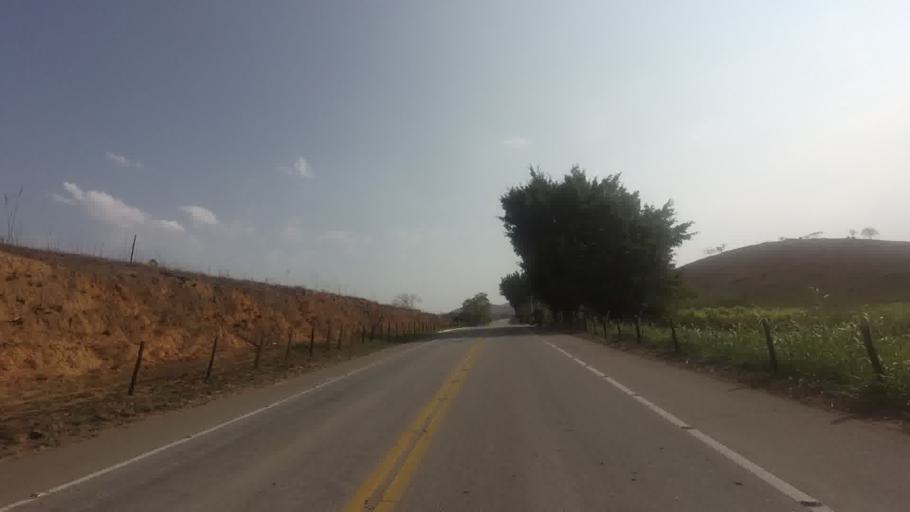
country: BR
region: Rio de Janeiro
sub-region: Bom Jesus Do Itabapoana
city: Bom Jesus do Itabapoana
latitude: -21.1316
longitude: -41.6486
